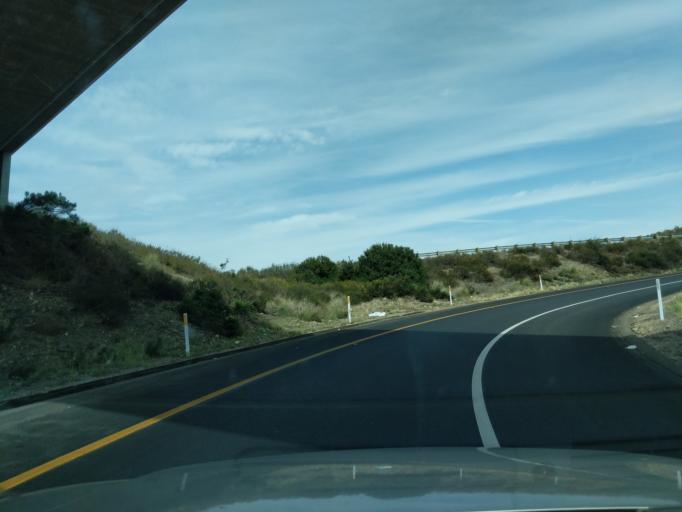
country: US
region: California
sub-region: San Diego County
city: La Mesa
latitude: 32.8430
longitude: -117.1194
